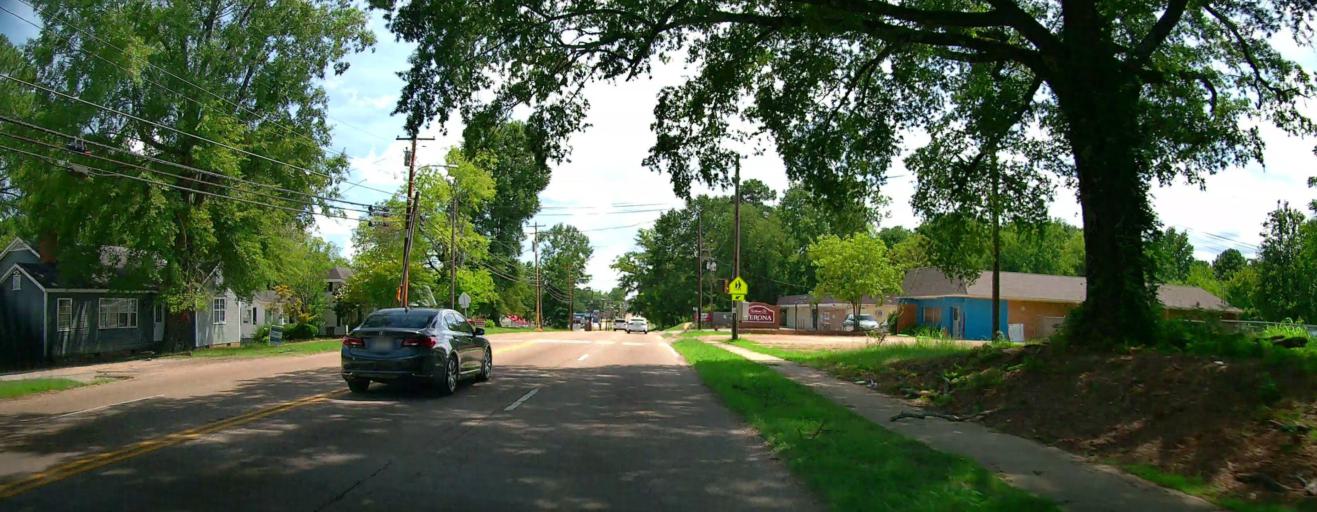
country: US
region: Mississippi
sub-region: Lee County
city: Verona
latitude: 34.2019
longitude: -88.7201
